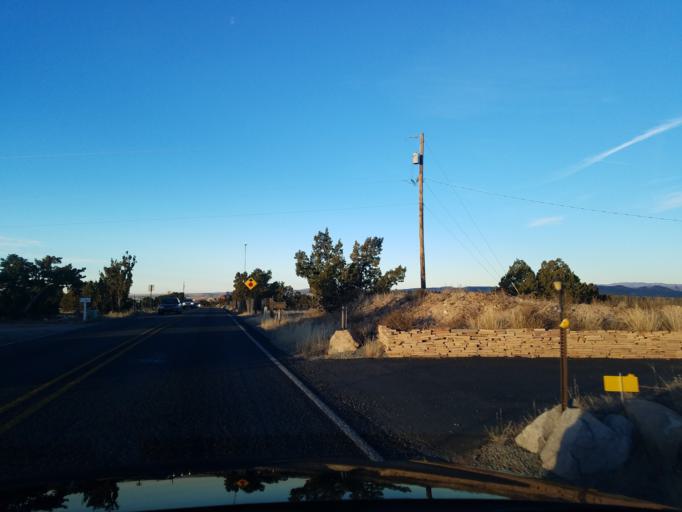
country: US
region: New Mexico
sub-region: Santa Fe County
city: Agua Fria
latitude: 35.6697
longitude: -106.0074
